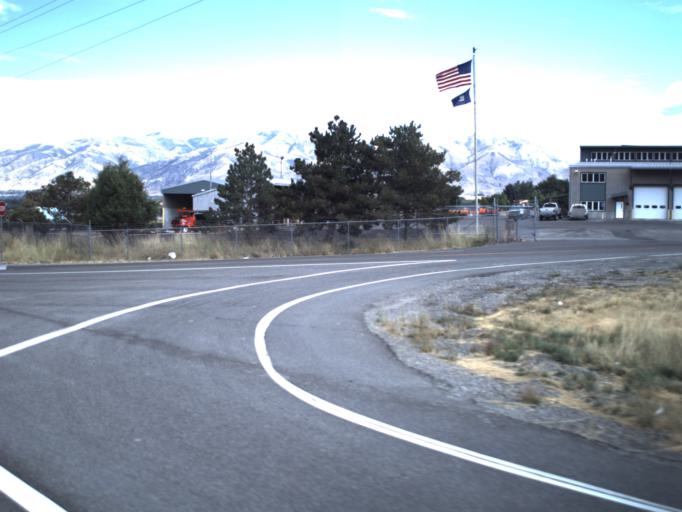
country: US
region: Utah
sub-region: Cache County
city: Wellsville
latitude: 41.6156
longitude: -111.9337
